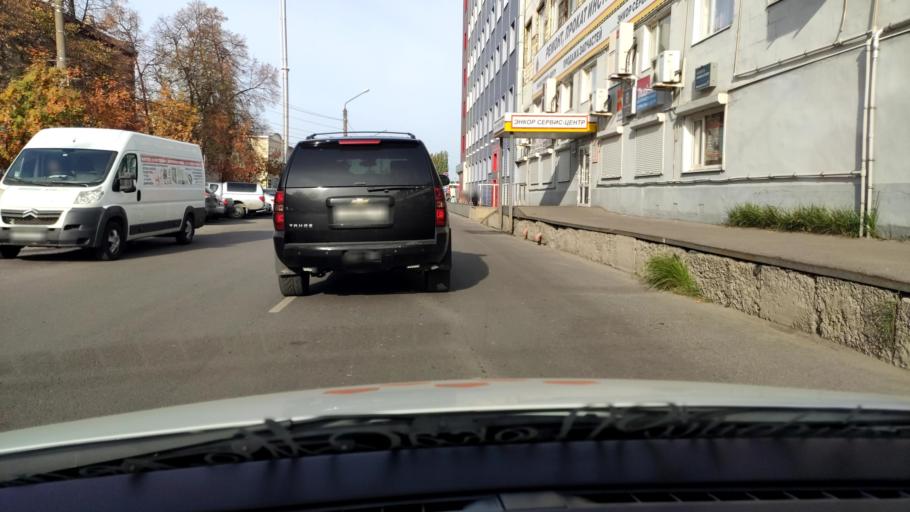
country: RU
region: Voronezj
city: Voronezh
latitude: 51.6802
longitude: 39.1732
